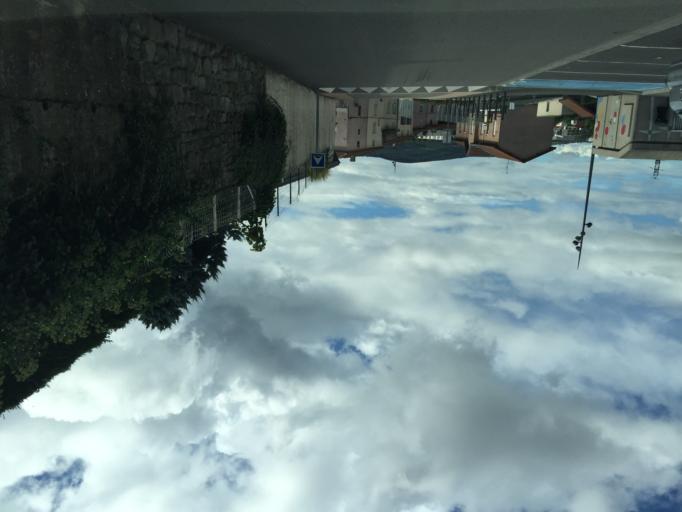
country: FR
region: Rhone-Alpes
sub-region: Departement de la Loire
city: Lorette
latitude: 45.5211
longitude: 4.5881
